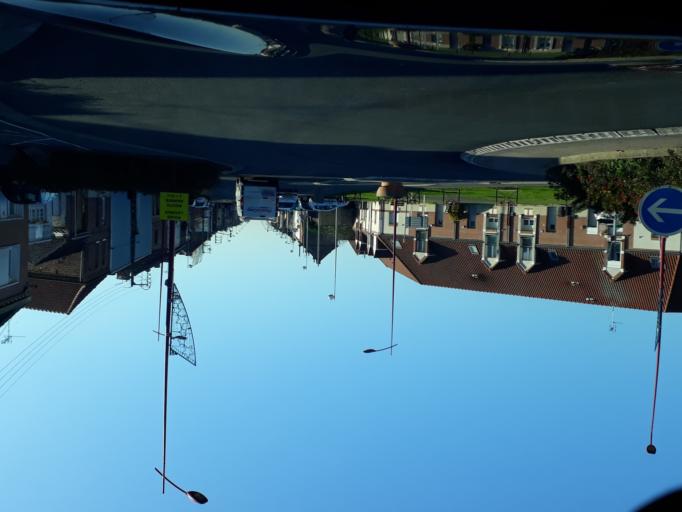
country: FR
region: Nord-Pas-de-Calais
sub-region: Departement du Nord
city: Aniche
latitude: 50.3297
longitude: 3.2435
